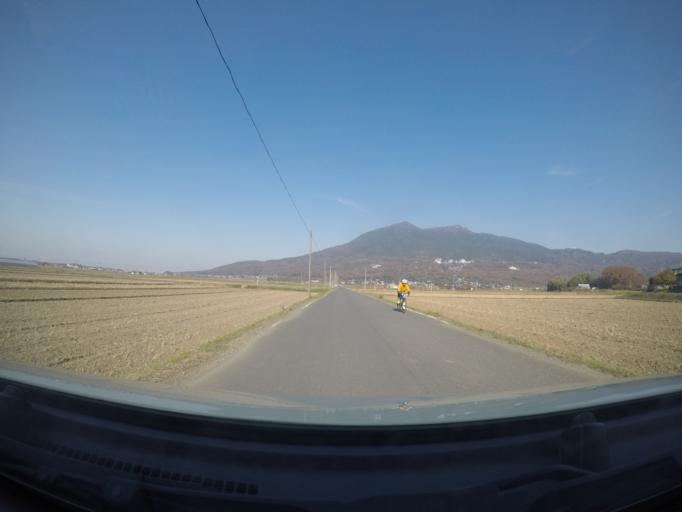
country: JP
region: Ibaraki
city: Tsukuba
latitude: 36.1919
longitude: 140.0895
